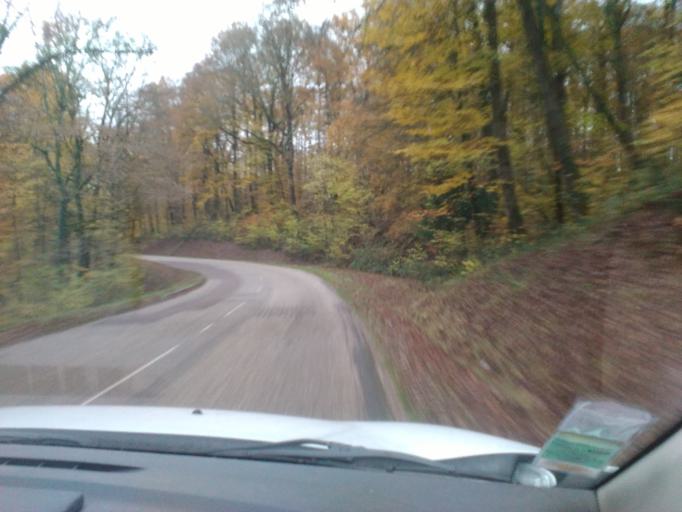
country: FR
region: Lorraine
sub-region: Departement des Vosges
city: Darnieulles
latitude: 48.2378
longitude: 6.2839
